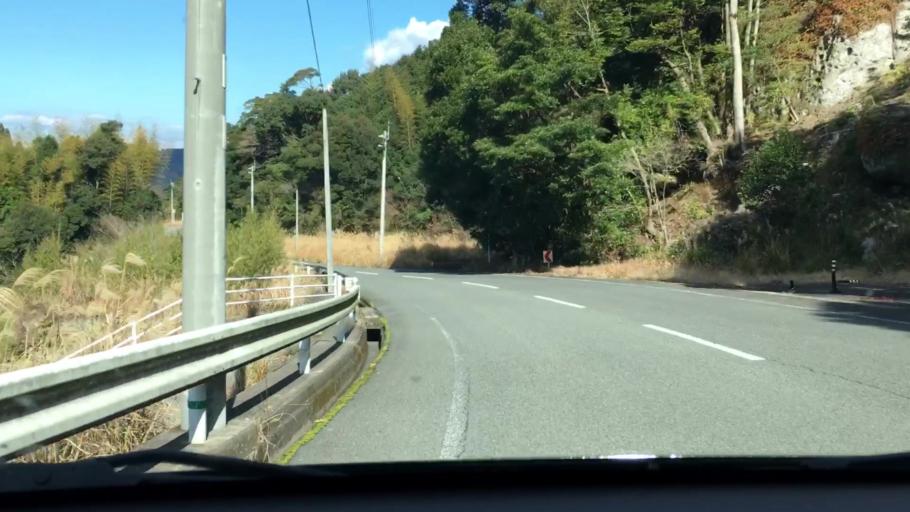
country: JP
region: Kagoshima
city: Ijuin
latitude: 31.7193
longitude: 130.4158
